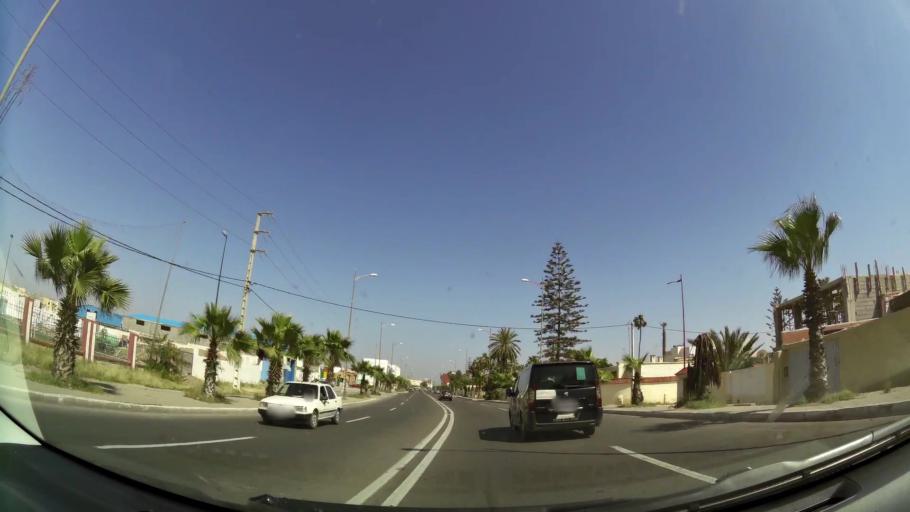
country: MA
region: Souss-Massa-Draa
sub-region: Inezgane-Ait Mellou
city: Inezgane
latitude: 30.3649
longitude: -9.5423
